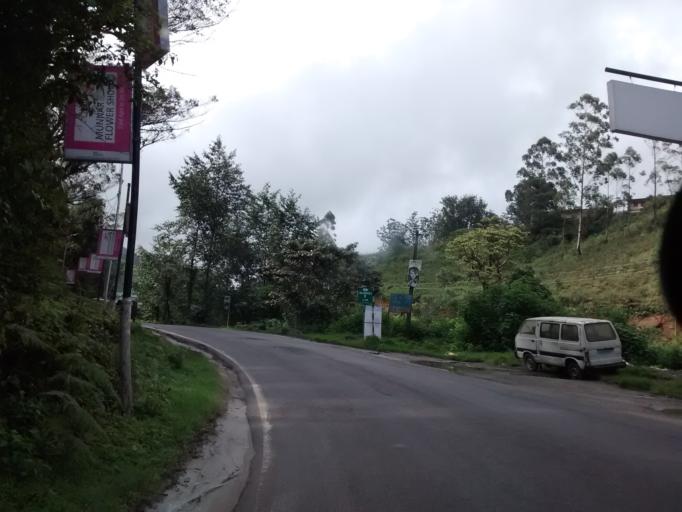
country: IN
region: Kerala
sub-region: Idukki
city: Munnar
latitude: 10.0821
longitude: 77.0620
